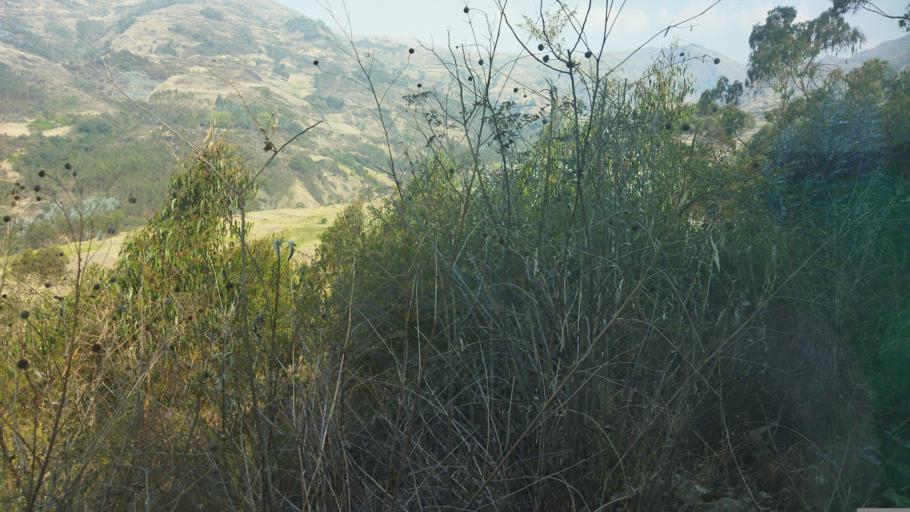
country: BO
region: La Paz
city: Quime
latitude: -16.9822
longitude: -67.1948
